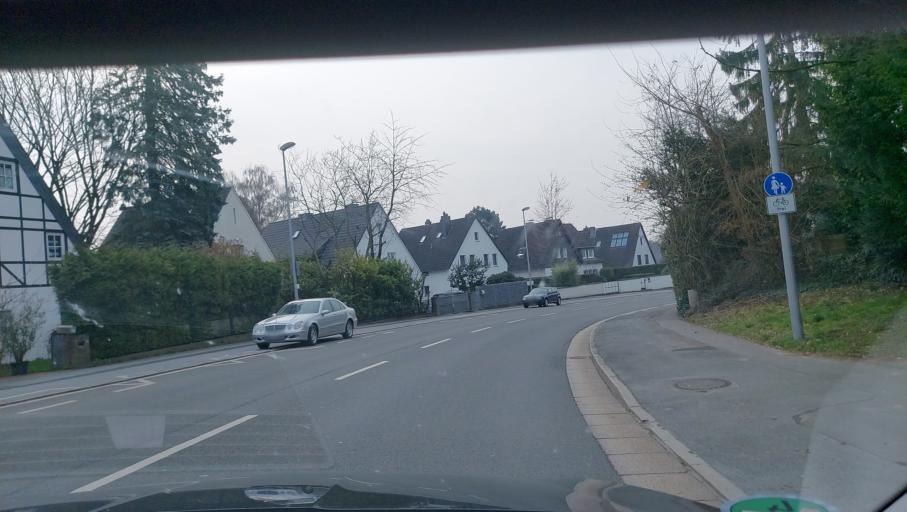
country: DE
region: North Rhine-Westphalia
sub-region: Regierungsbezirk Dusseldorf
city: Ratingen
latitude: 51.2479
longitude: 6.8628
